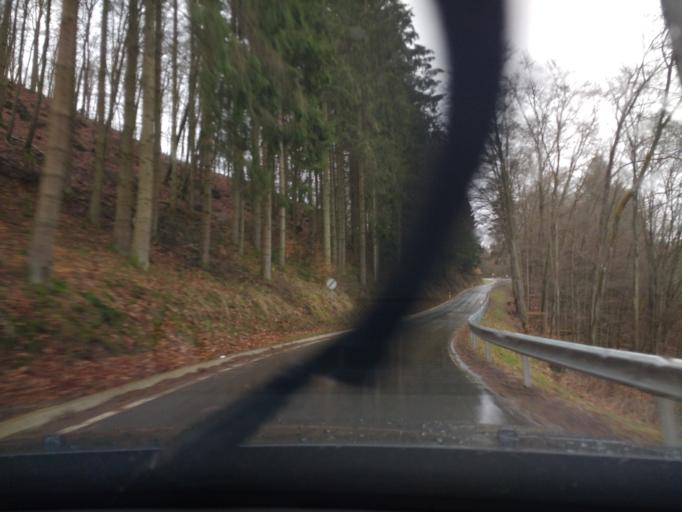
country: DE
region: Rheinland-Pfalz
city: Lotzbeuren
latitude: 49.9349
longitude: 7.2033
